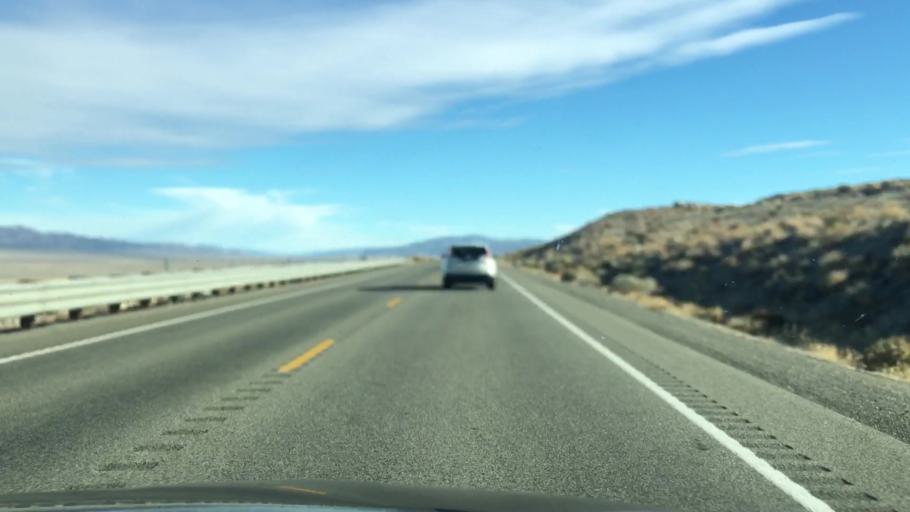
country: US
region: Nevada
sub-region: Mineral County
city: Hawthorne
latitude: 38.6145
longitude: -118.7254
